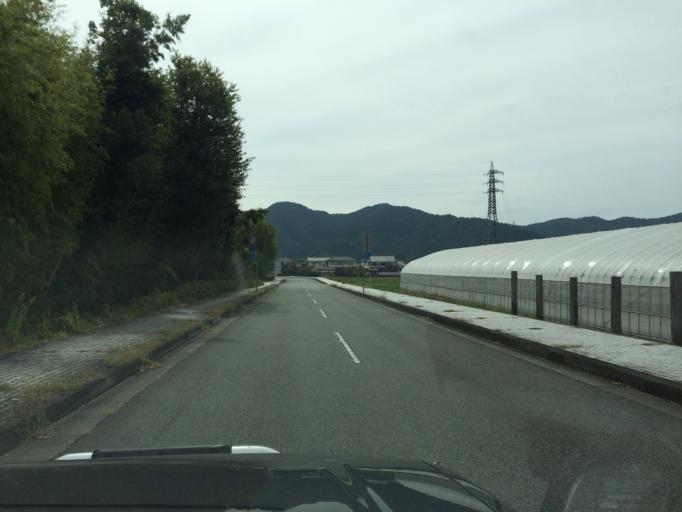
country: JP
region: Hyogo
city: Sasayama
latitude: 35.0730
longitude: 135.2135
